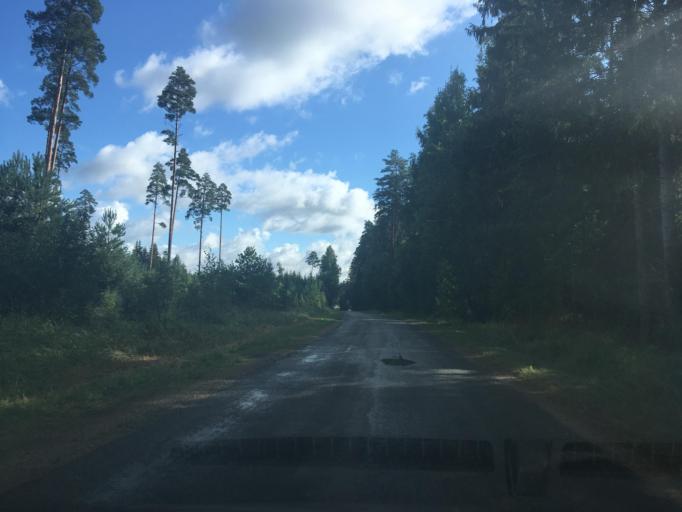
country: EE
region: Tartu
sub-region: Puhja vald
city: Puhja
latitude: 58.2336
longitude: 26.1598
